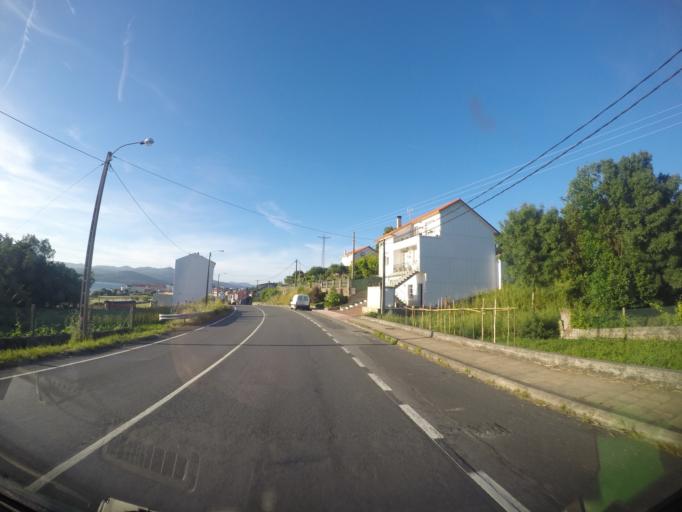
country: ES
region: Galicia
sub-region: Provincia da Coruna
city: Porto do Son
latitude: 42.7499
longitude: -8.9498
